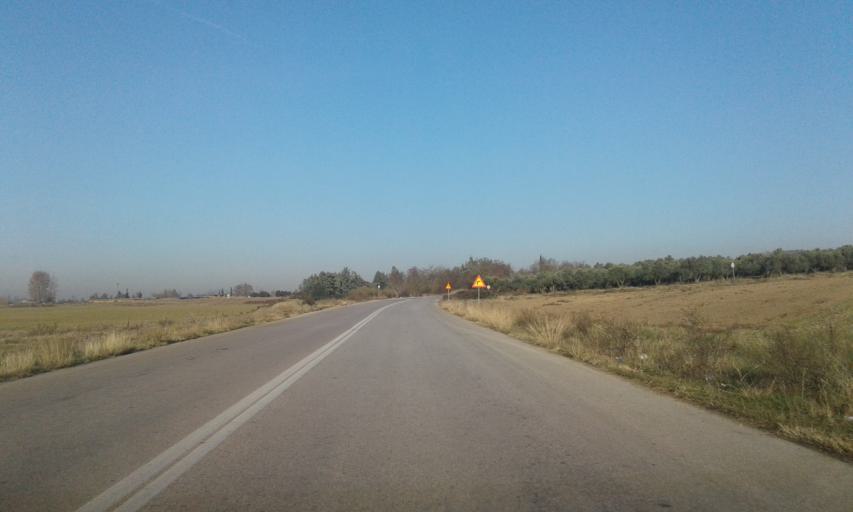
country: GR
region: Central Macedonia
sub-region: Nomos Thessalonikis
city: Kolchikon
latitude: 40.7101
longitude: 23.1810
